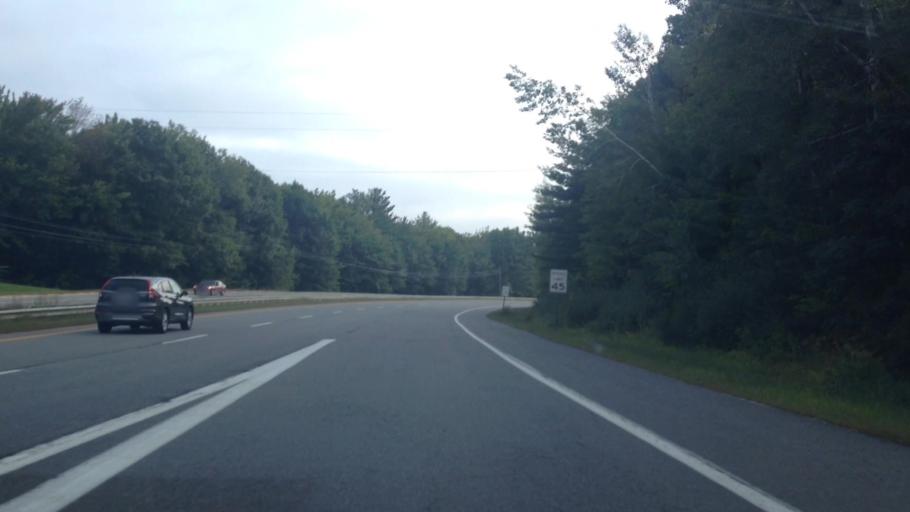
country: US
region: Maine
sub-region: Cumberland County
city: Westbrook
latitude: 43.6728
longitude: -70.3467
